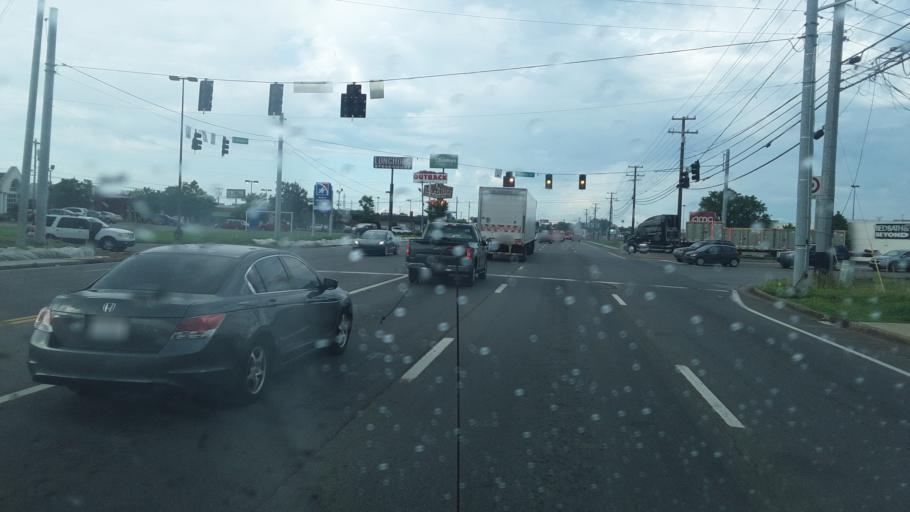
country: US
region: Tennessee
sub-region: Montgomery County
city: Clarksville
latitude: 36.5852
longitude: -87.2952
